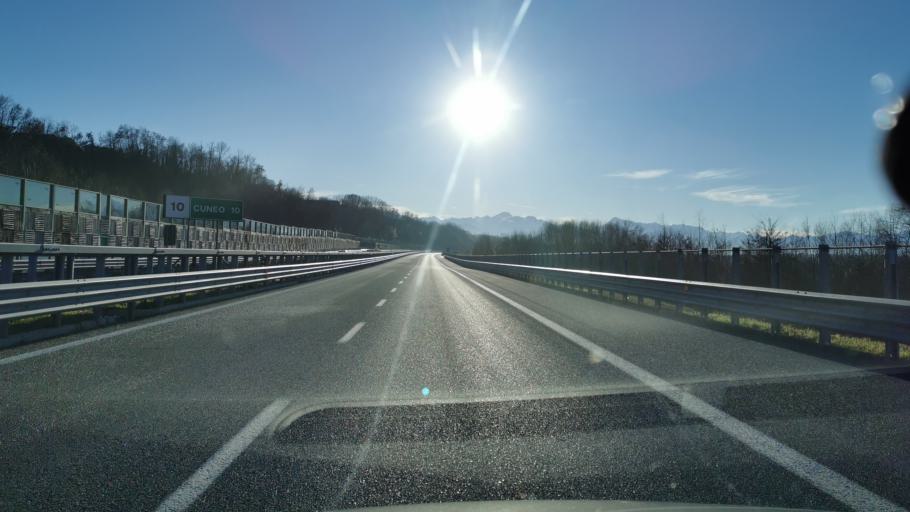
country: IT
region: Piedmont
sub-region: Provincia di Cuneo
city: Montanera
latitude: 44.4651
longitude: 7.6647
